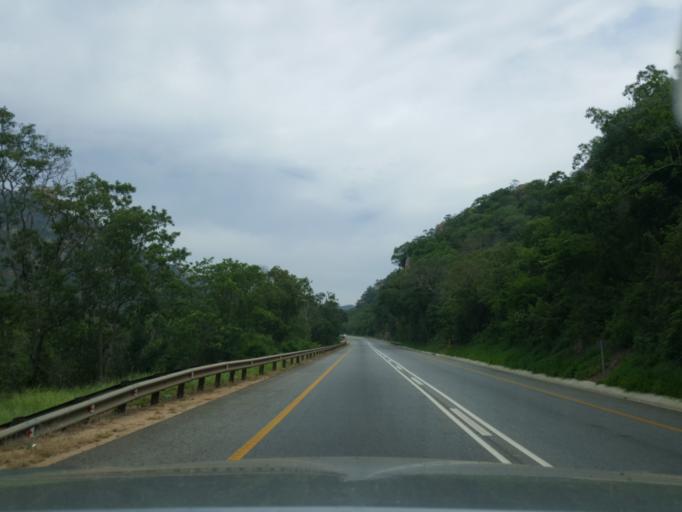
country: ZA
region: Mpumalanga
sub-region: Ehlanzeni District
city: Nelspruit
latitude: -25.5118
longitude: 31.2149
